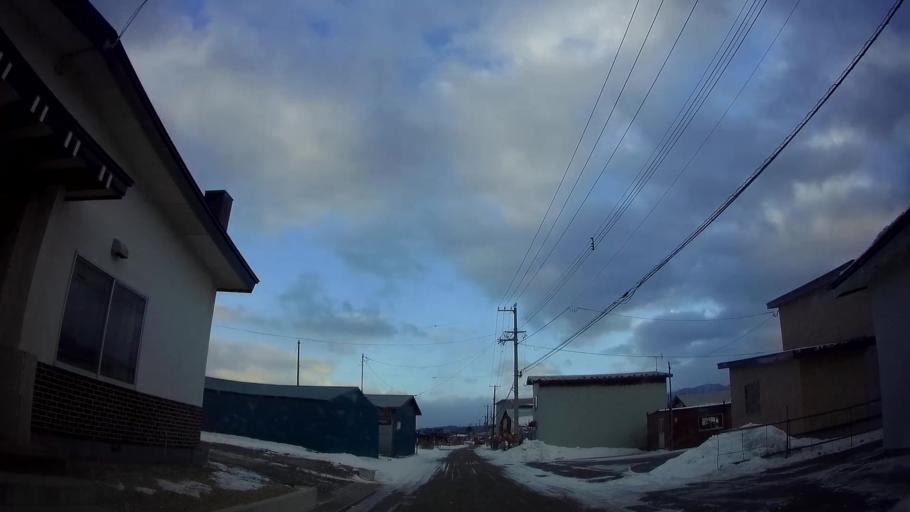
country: JP
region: Hokkaido
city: Nanae
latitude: 42.0425
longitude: 140.8139
